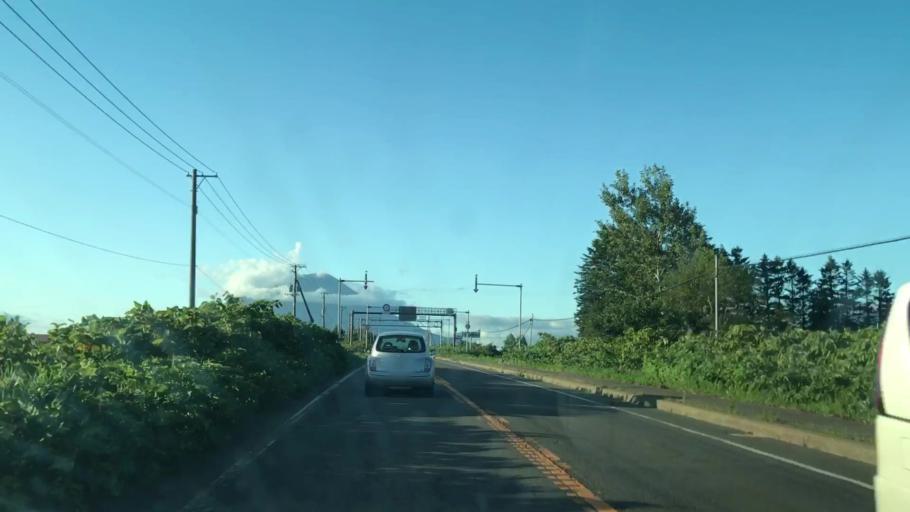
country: JP
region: Hokkaido
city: Niseko Town
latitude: 42.6708
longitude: 140.8424
